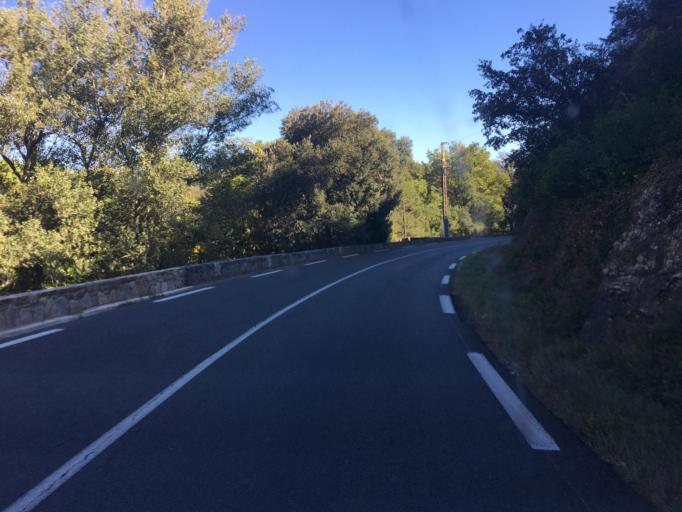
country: FR
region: Languedoc-Roussillon
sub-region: Departement de l'Herault
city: Nebian
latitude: 43.6110
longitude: 3.3941
